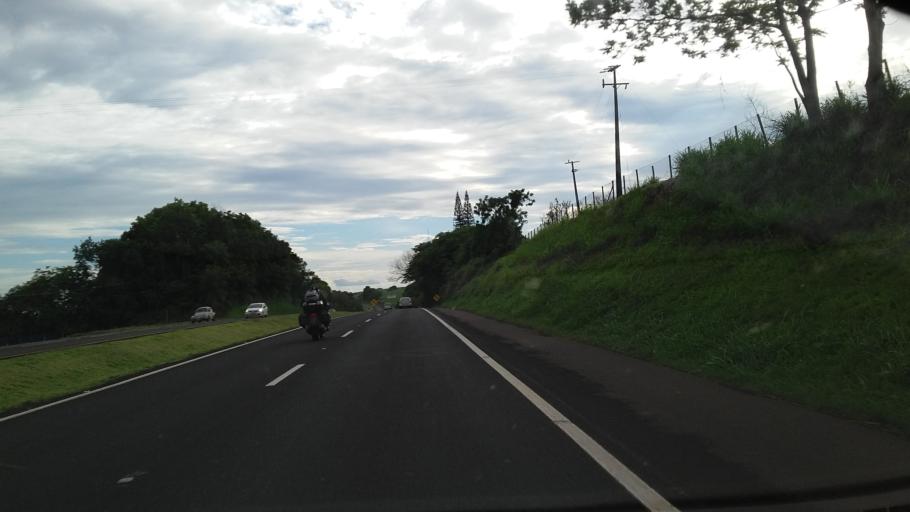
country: BR
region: Parana
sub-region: Paicandu
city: Paicandu
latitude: -23.5078
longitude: -52.0223
